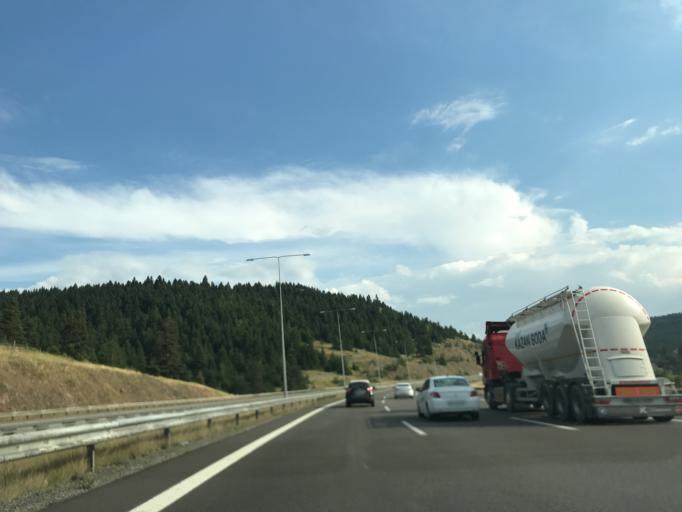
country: TR
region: Ankara
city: Pecenek
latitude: 40.5955
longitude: 32.2874
